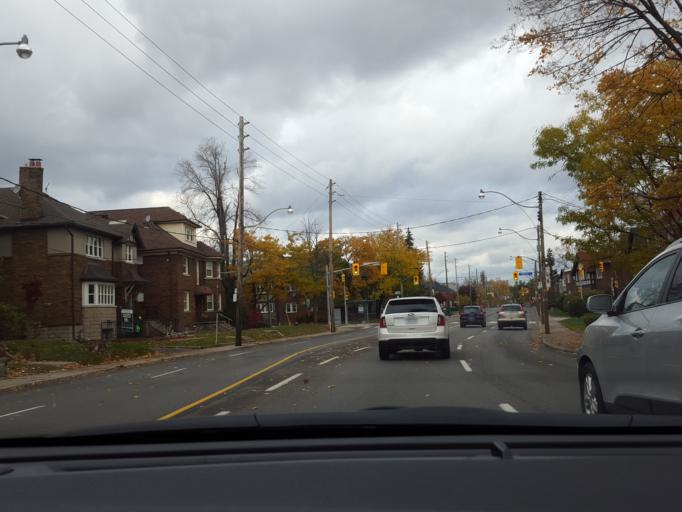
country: CA
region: Ontario
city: Toronto
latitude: 43.7114
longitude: -79.4116
